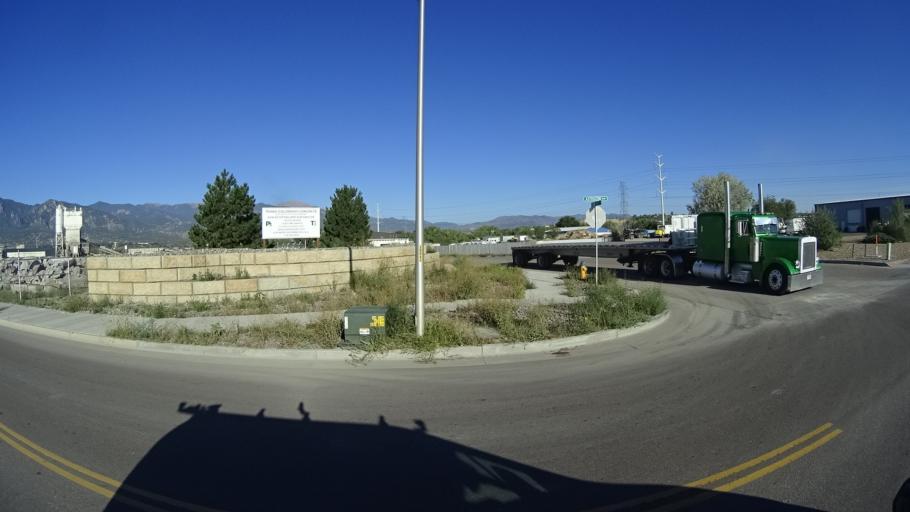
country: US
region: Colorado
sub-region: El Paso County
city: Stratmoor
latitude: 38.7875
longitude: -104.7647
